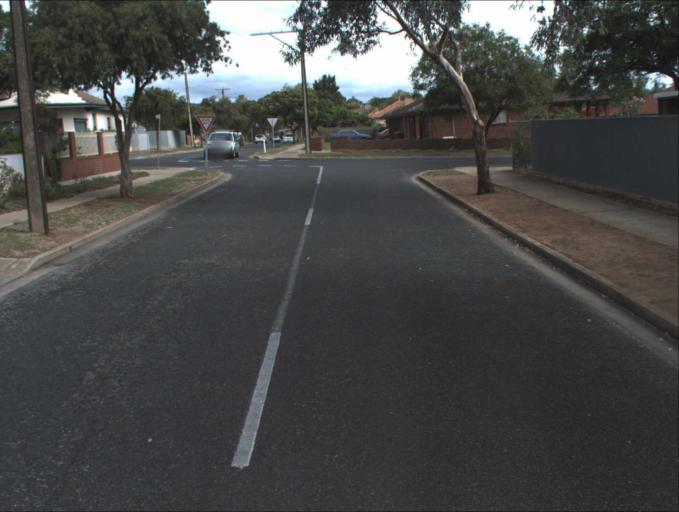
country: AU
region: South Australia
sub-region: Port Adelaide Enfield
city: Blair Athol
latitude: -34.8652
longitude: 138.5961
